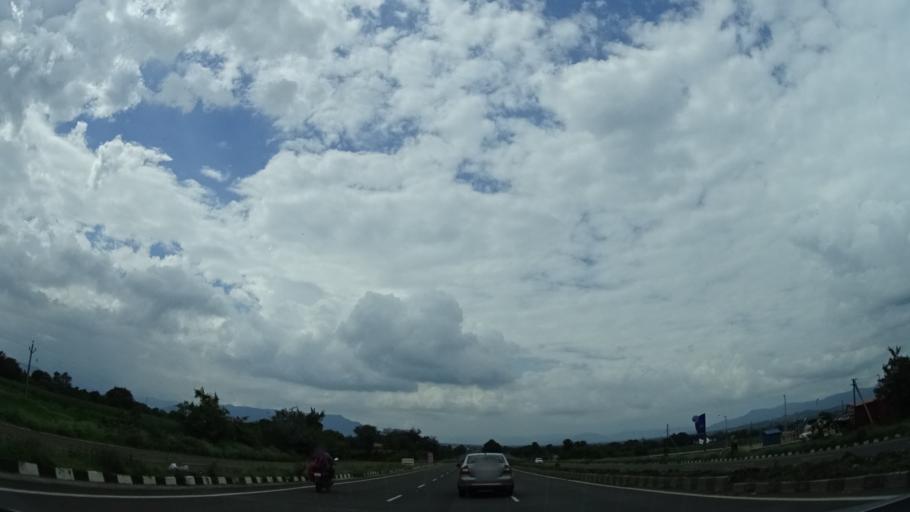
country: IN
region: Maharashtra
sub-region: Satara Division
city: Satara
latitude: 17.7975
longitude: 73.9771
